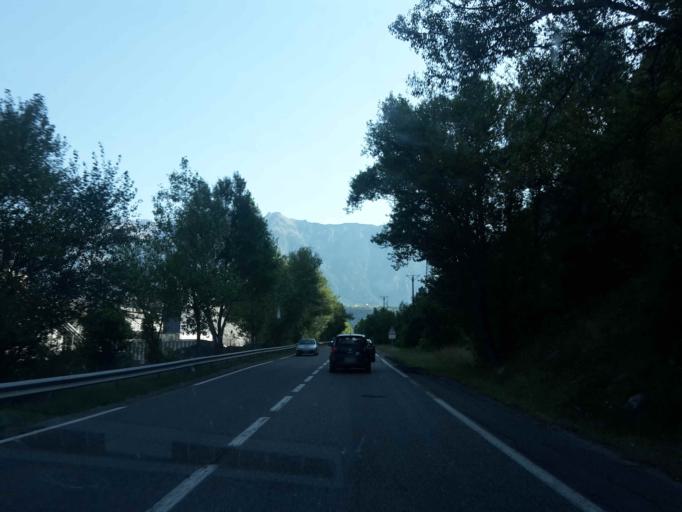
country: FR
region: Provence-Alpes-Cote d'Azur
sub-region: Departement des Hautes-Alpes
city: Guillestre
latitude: 44.6523
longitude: 6.5885
